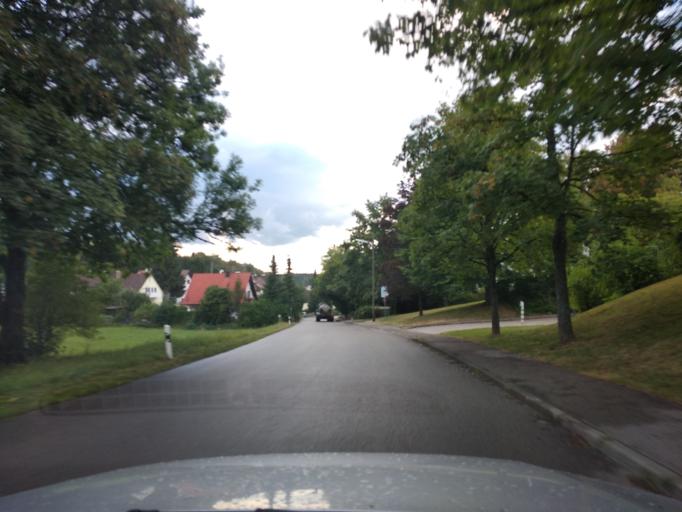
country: DE
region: Bavaria
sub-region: Swabia
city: Wolfertschwenden
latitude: 47.8695
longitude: 10.2226
